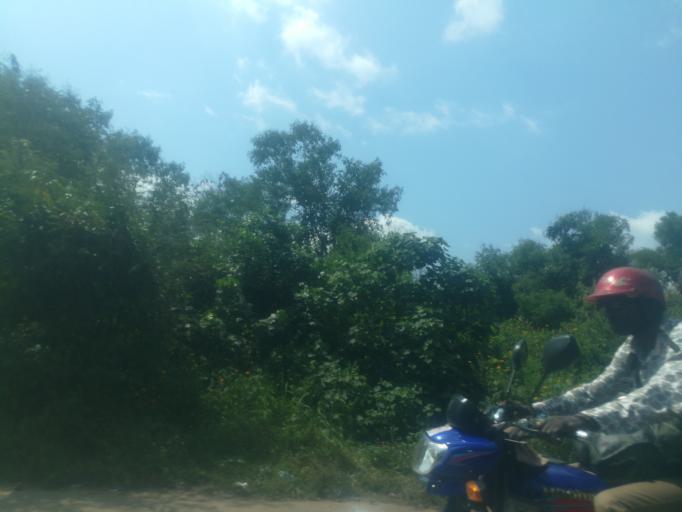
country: NG
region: Oyo
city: Moniya
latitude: 7.5759
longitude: 3.9147
